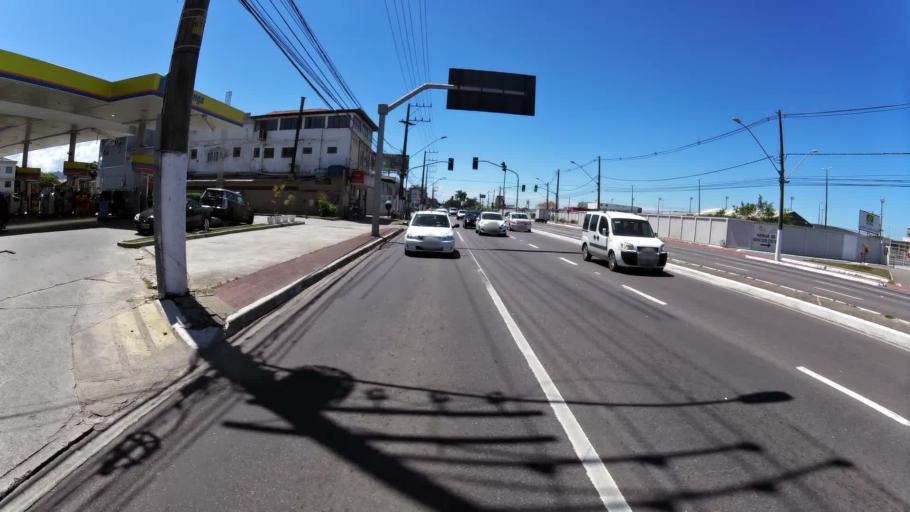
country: BR
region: Espirito Santo
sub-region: Vila Velha
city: Vila Velha
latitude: -20.2590
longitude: -40.2921
